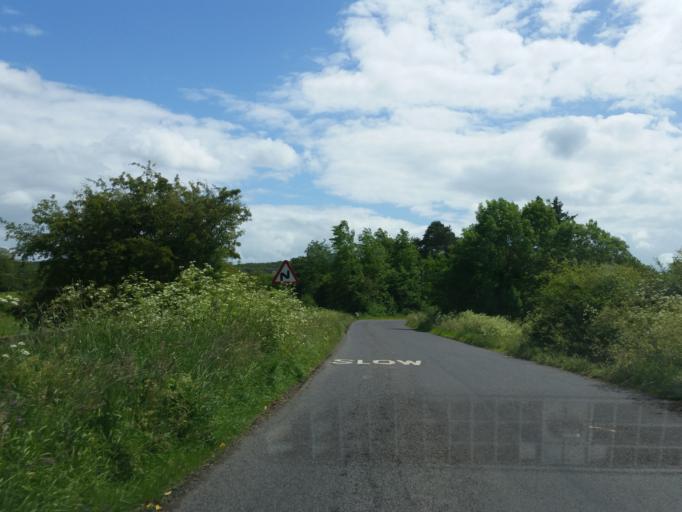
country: GB
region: Northern Ireland
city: Fivemiletown
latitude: 54.3657
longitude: -7.3102
